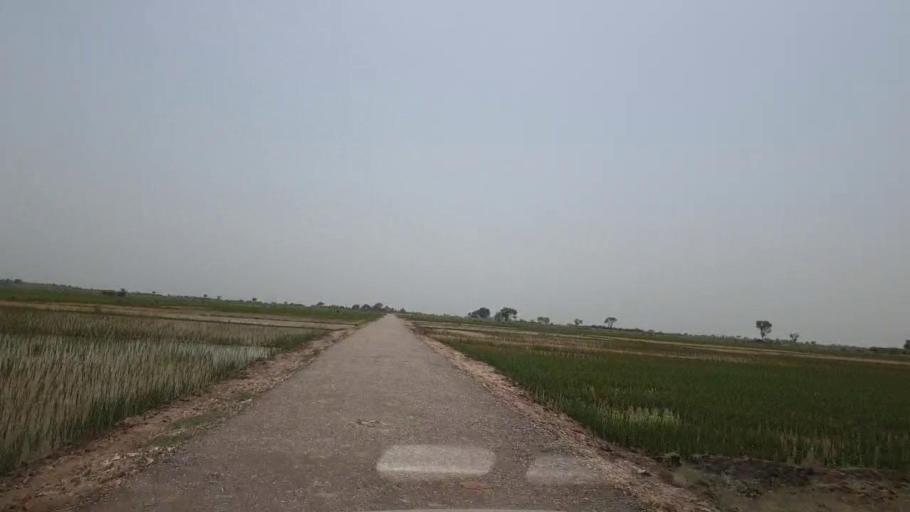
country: PK
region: Sindh
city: Garhi Yasin
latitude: 28.0627
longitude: 68.3188
